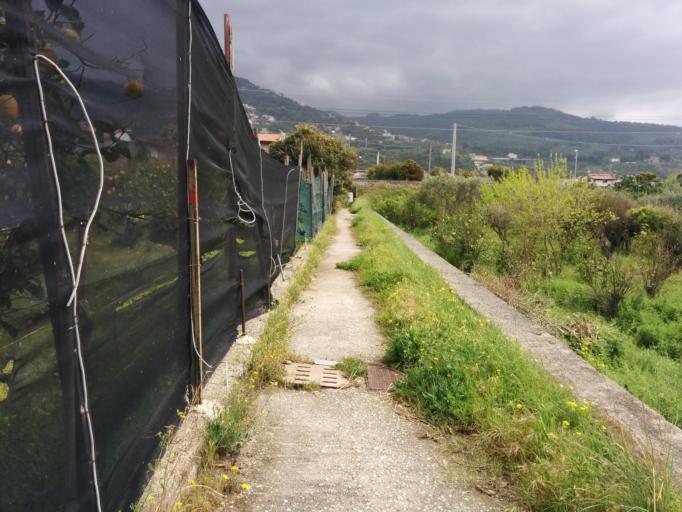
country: IT
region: Sicily
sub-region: Messina
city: Capo d'Orlando
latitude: 38.1417
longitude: 14.7250
